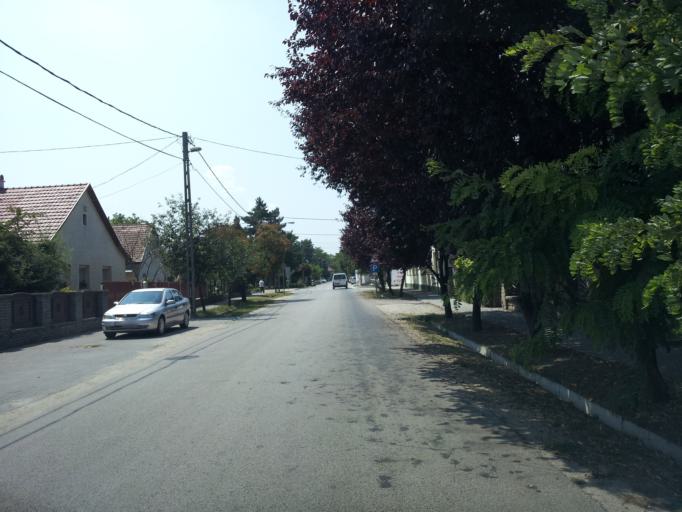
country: HU
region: Pest
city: Dunavarsany
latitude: 47.2777
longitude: 19.0687
